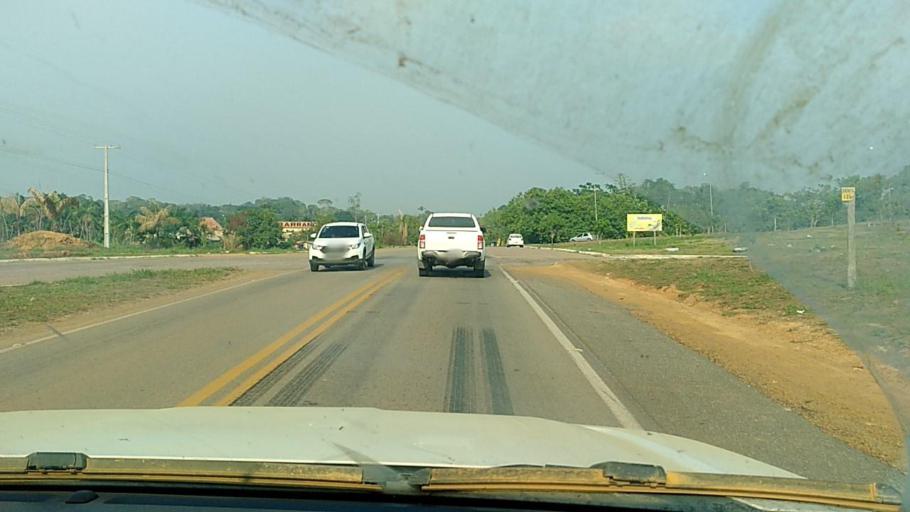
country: BR
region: Rondonia
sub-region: Porto Velho
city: Porto Velho
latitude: -8.7395
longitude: -63.9340
